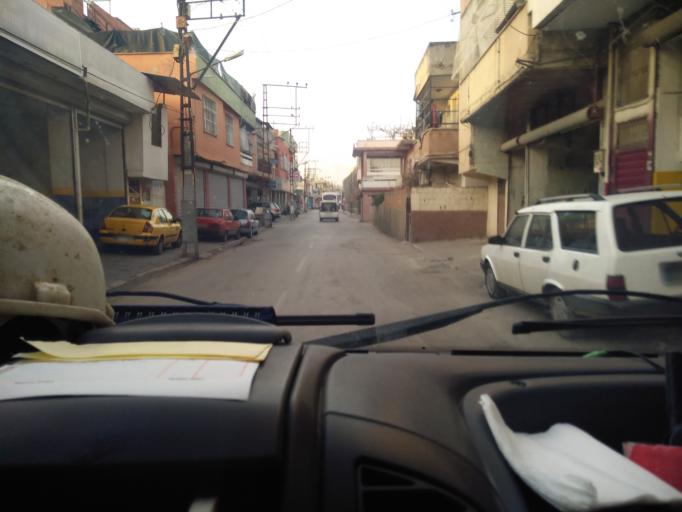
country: TR
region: Adana
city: Seyhan
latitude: 36.9982
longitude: 35.2798
